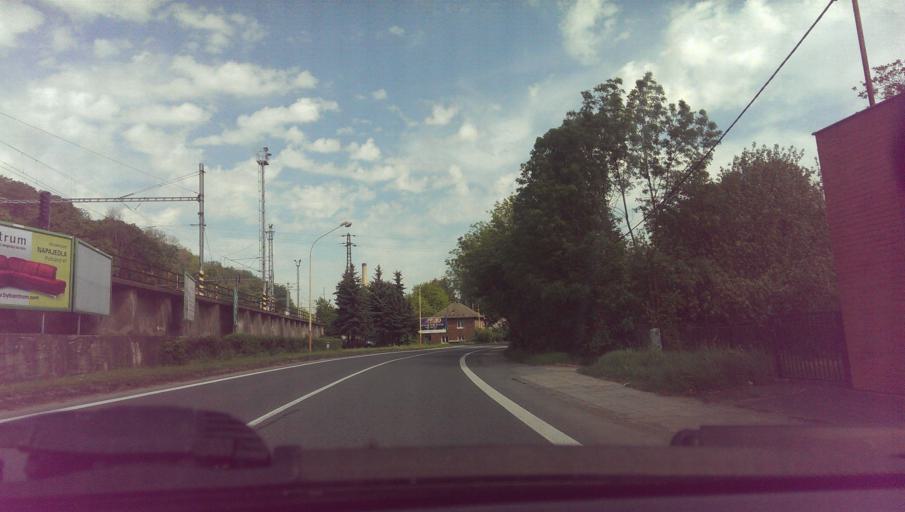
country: CZ
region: Zlin
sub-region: Okres Zlin
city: Napajedla
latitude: 49.1645
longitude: 17.5050
